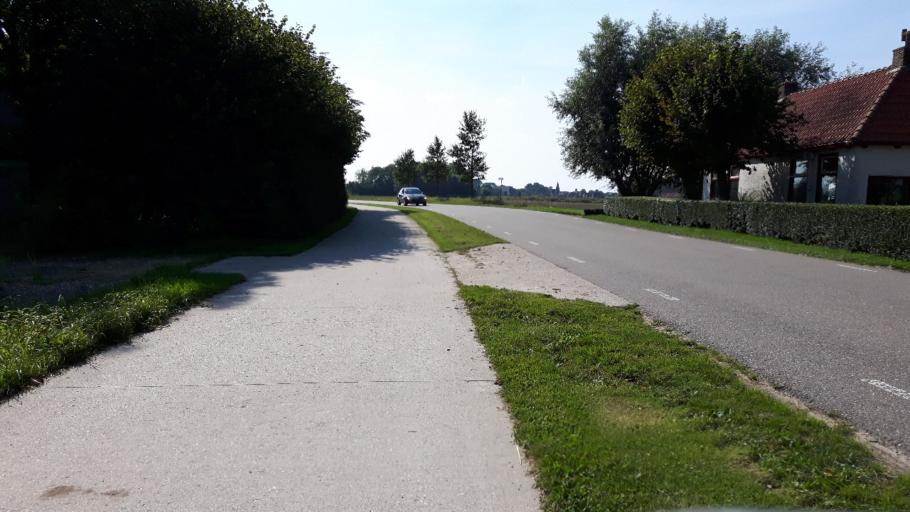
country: NL
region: Friesland
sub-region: Gemeente Franekeradeel
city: Tzummarum
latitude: 53.2116
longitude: 5.5590
